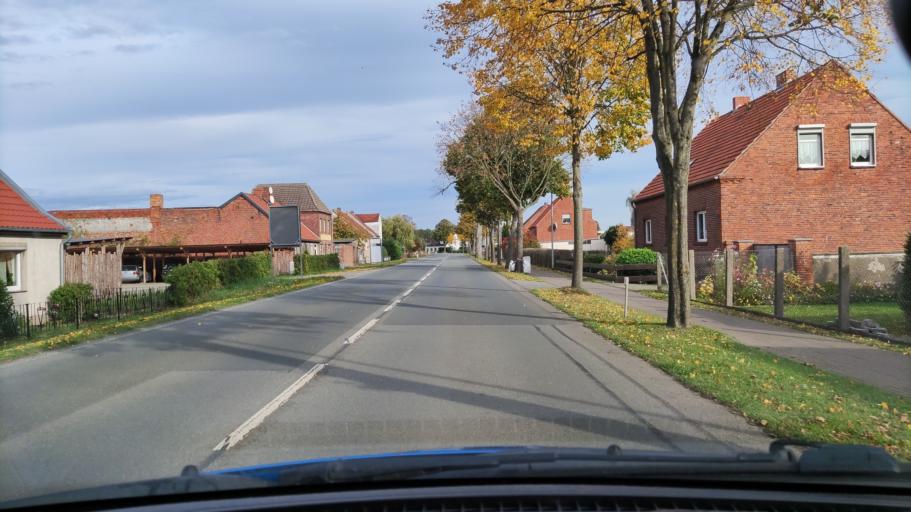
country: DE
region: Brandenburg
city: Weisen
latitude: 53.0251
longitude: 11.7895
